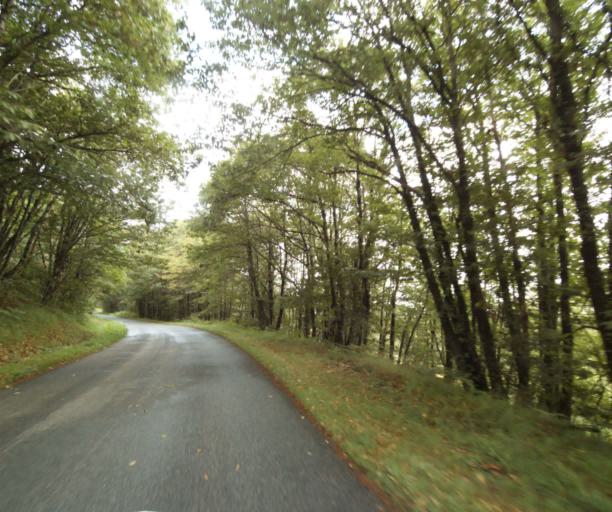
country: FR
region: Limousin
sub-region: Departement de la Correze
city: Sainte-Fortunade
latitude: 45.1943
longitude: 1.7853
